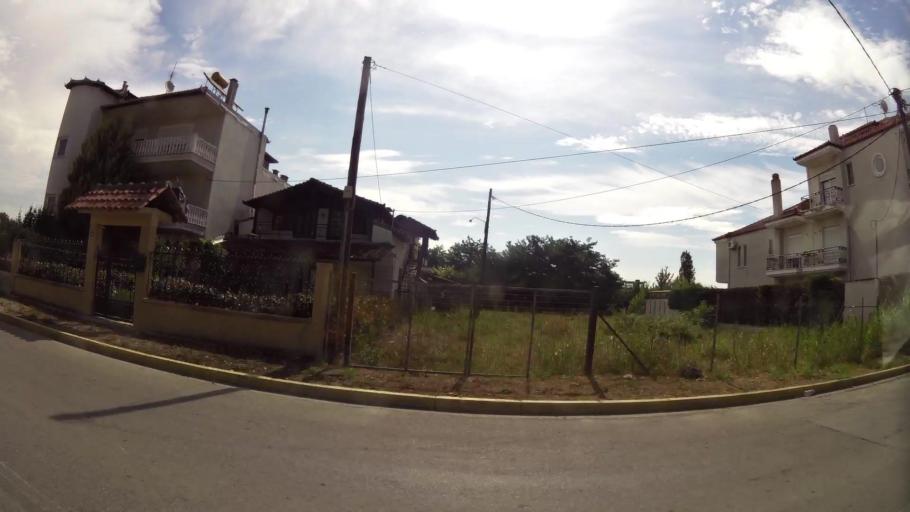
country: GR
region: Central Macedonia
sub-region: Nomos Pierias
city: Katerini
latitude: 40.2856
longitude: 22.5033
